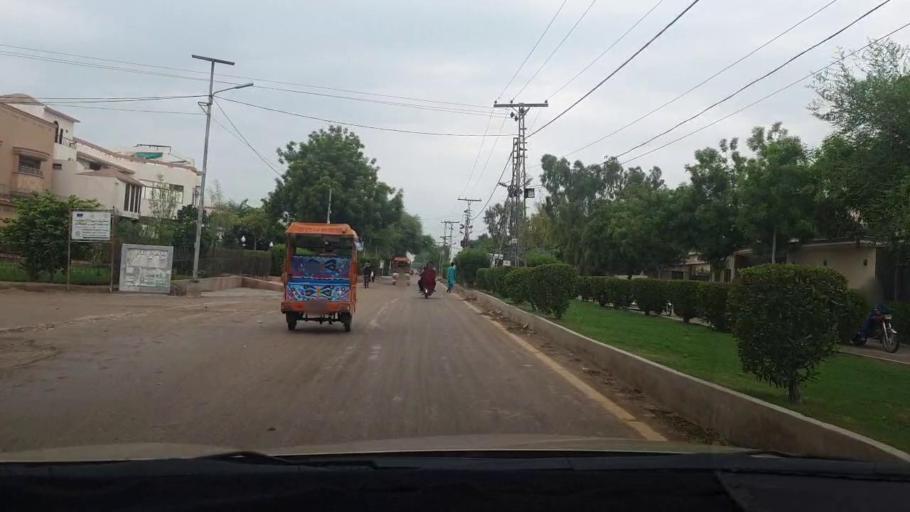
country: PK
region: Sindh
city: Larkana
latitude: 27.5618
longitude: 68.1973
